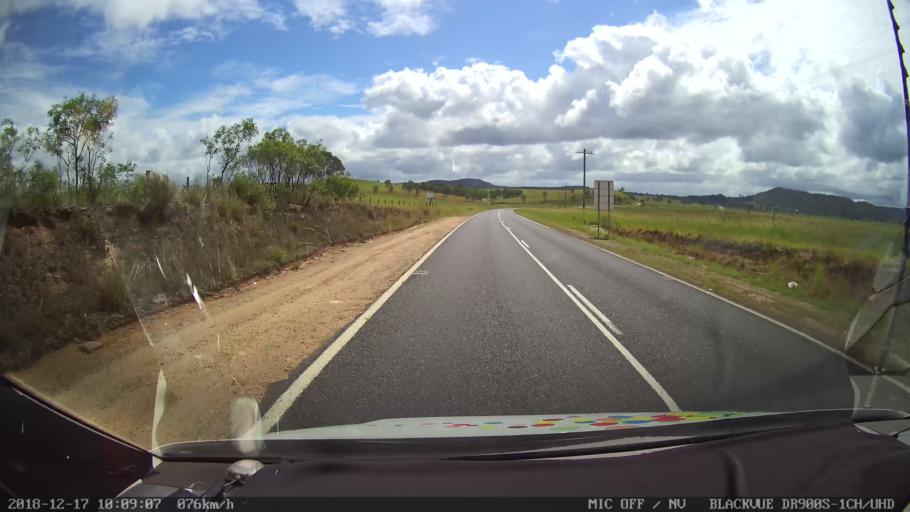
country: AU
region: New South Wales
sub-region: Tenterfield Municipality
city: Carrolls Creek
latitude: -28.8882
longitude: 152.5395
